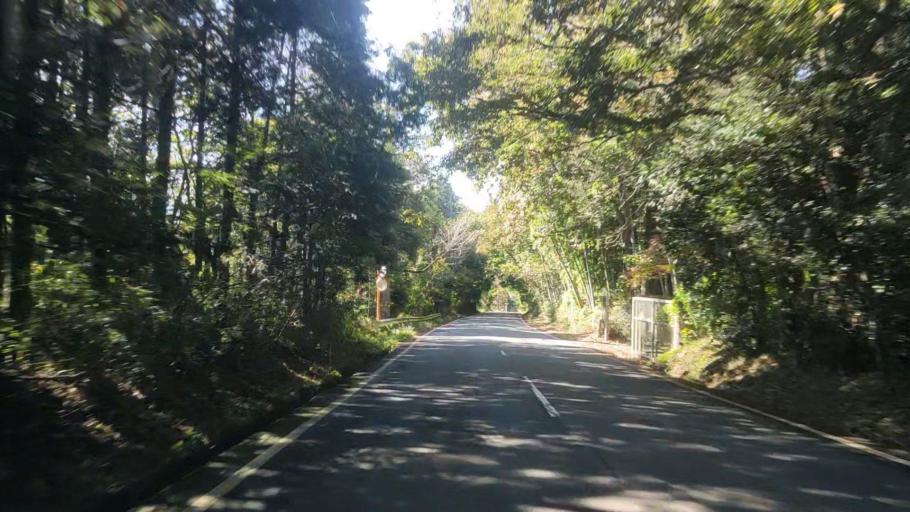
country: JP
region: Shizuoka
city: Atami
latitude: 35.0342
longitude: 139.0156
